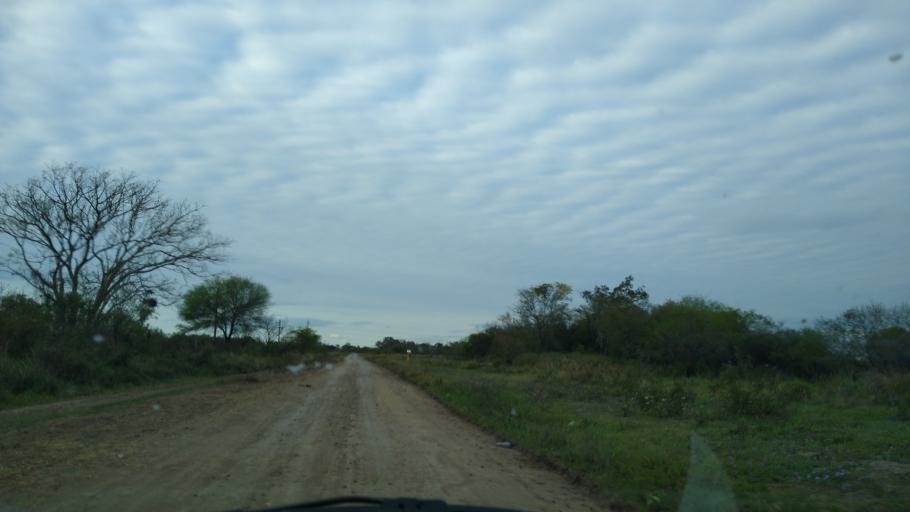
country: AR
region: Chaco
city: Puerto Tirol
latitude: -27.3899
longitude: -59.0491
